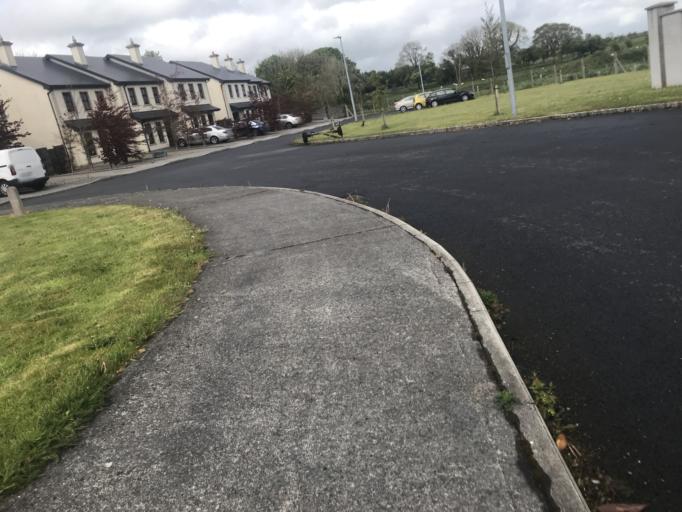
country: IE
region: Connaught
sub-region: County Galway
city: Moycullen
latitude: 53.4684
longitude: -9.0982
